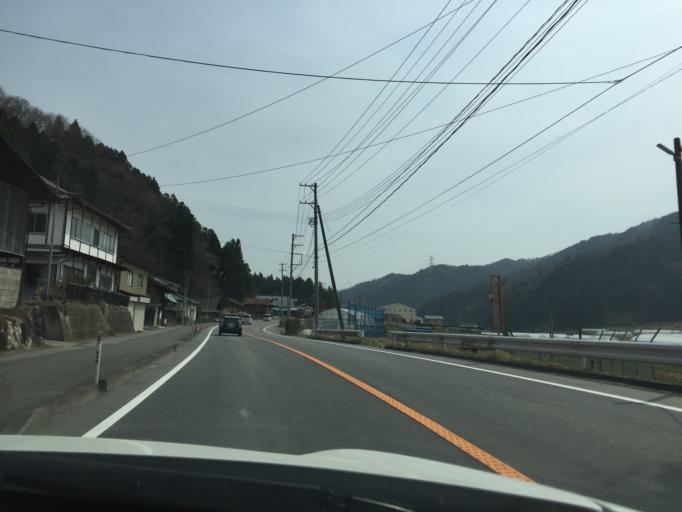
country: JP
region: Fukushima
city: Ishikawa
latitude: 37.1131
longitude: 140.5049
